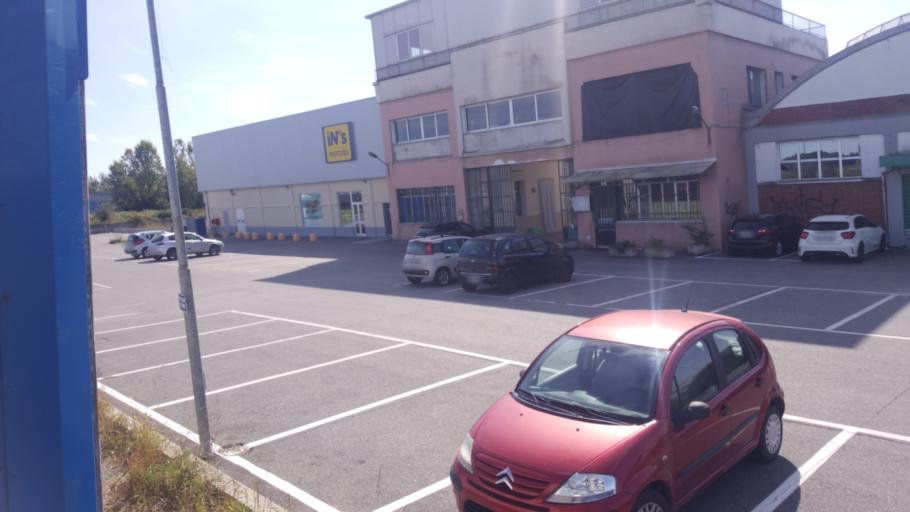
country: IT
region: Piedmont
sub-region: Provincia di Vercelli
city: Trino
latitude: 45.1962
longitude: 8.2820
